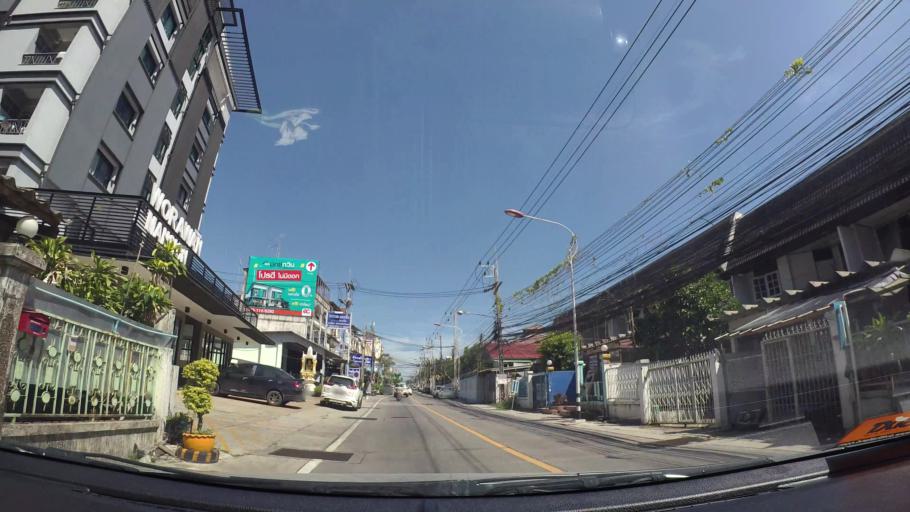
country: TH
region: Chon Buri
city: Si Racha
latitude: 13.1608
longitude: 100.9307
